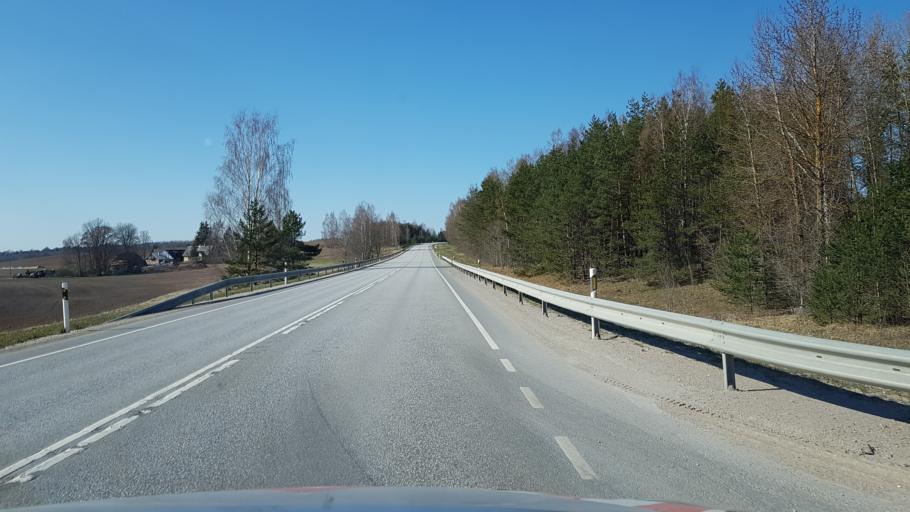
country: EE
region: Tartu
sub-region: Tartu linn
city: Tartu
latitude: 58.4753
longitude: 26.7849
